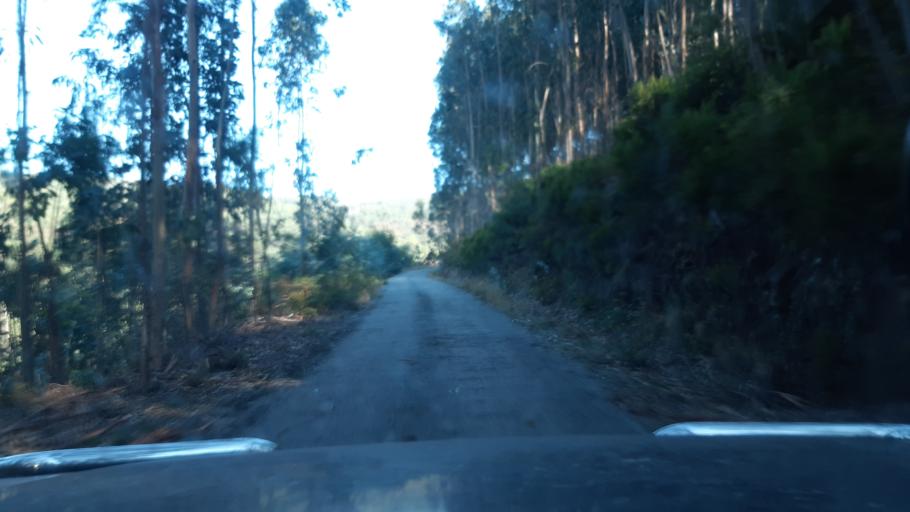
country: PT
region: Viseu
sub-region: Mortagua
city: Mortagua
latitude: 40.5235
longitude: -8.2533
